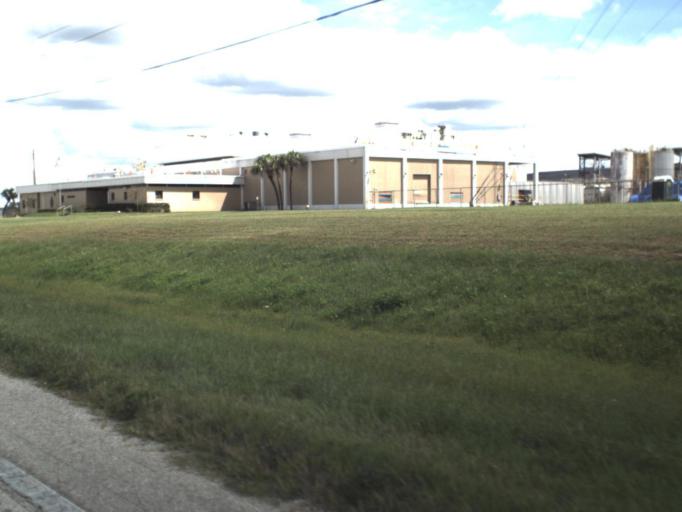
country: US
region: Florida
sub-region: Polk County
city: Bartow
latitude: 27.8983
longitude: -81.8997
